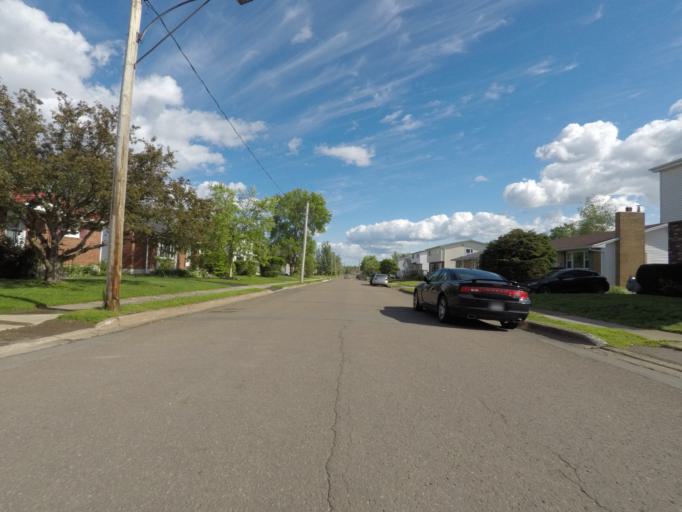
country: CA
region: New Brunswick
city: Moncton
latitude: 46.0980
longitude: -64.8254
